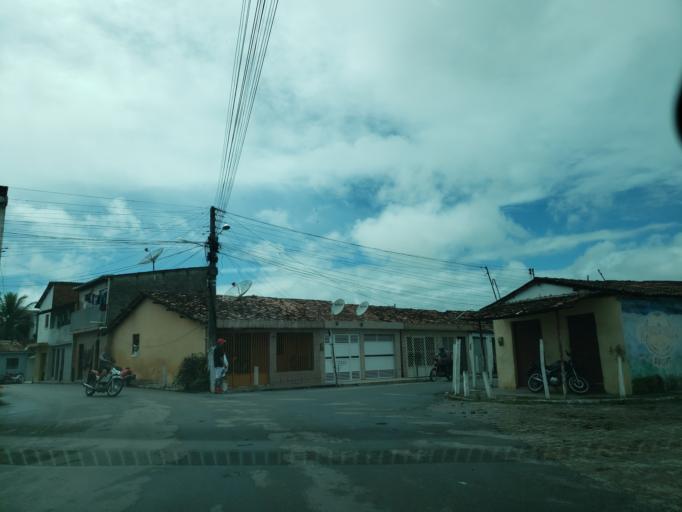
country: BR
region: Alagoas
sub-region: Uniao Dos Palmares
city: Uniao dos Palmares
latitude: -9.1609
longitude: -36.0266
